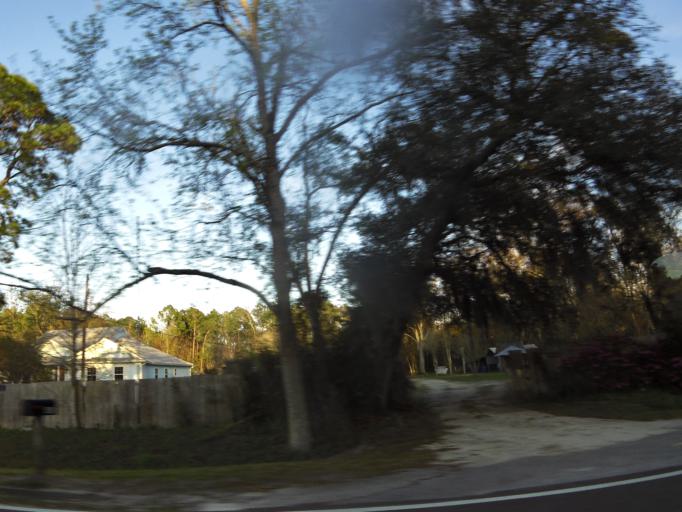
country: US
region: Florida
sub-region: Duval County
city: Jacksonville
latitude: 30.4661
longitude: -81.6424
